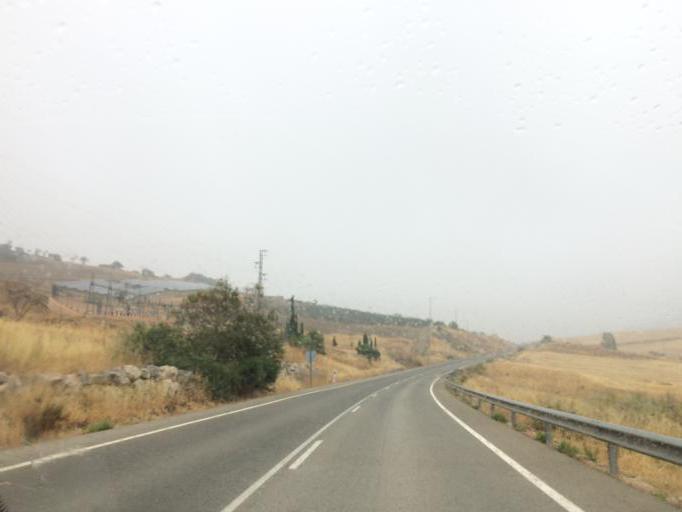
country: ES
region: Andalusia
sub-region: Provincia de Malaga
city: Casabermeja
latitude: 36.9006
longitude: -4.4234
